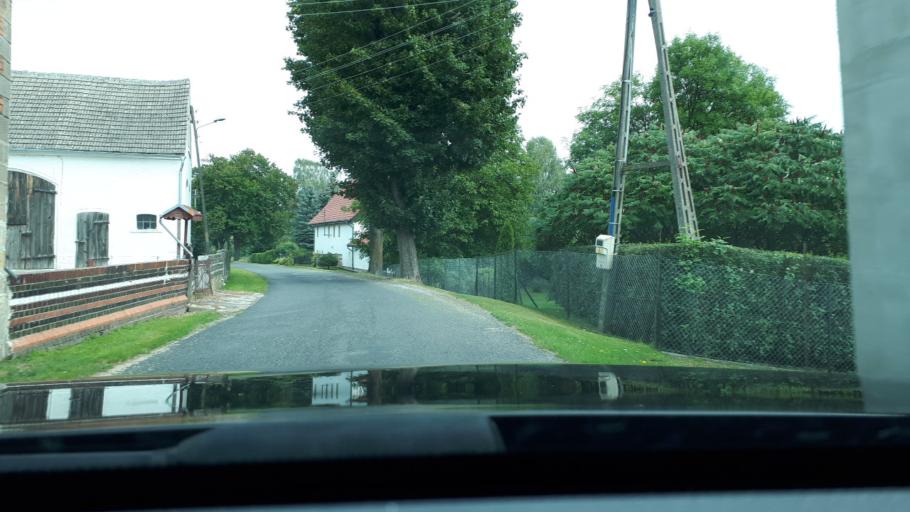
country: PL
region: Lower Silesian Voivodeship
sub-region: Powiat zlotoryjski
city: Olszanica
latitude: 51.2312
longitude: 15.8036
